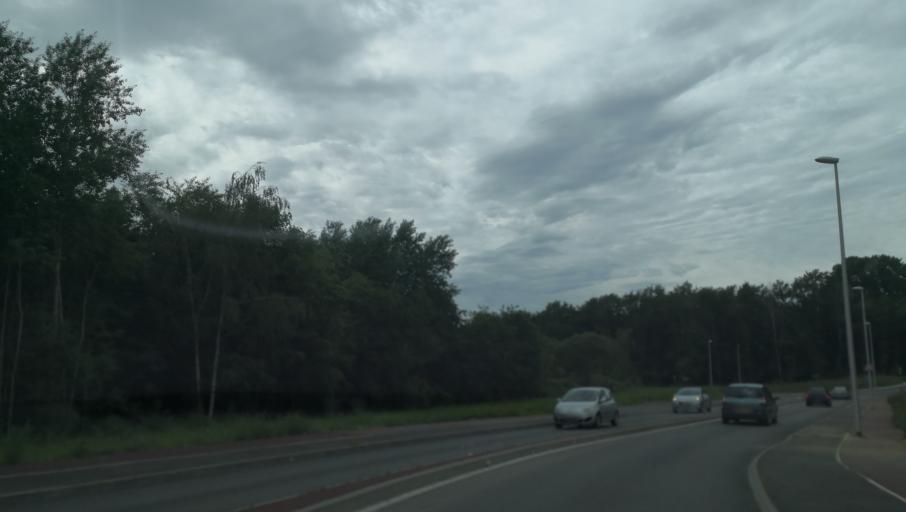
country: FR
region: Limousin
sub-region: Departement de la Haute-Vienne
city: Couzeix
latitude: 45.8668
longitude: 1.2608
